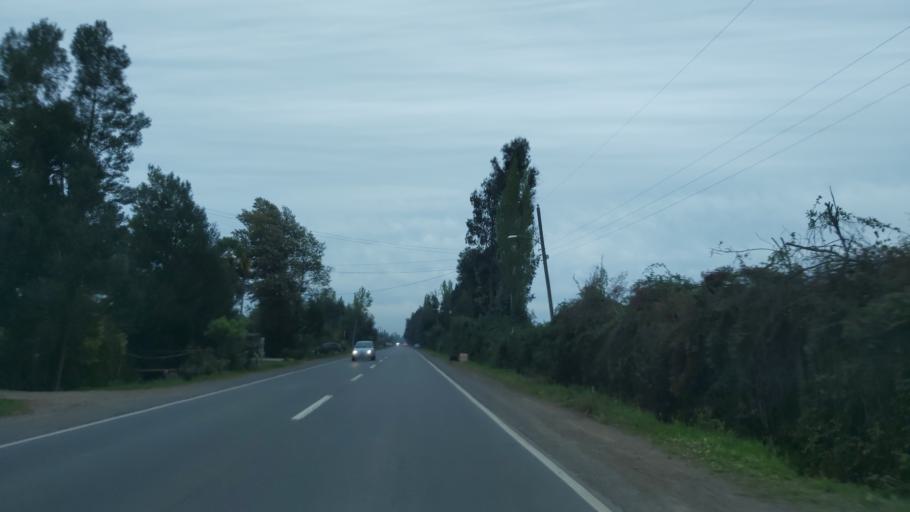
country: CL
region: Maule
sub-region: Provincia de Linares
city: Colbun
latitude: -35.7351
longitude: -71.4895
